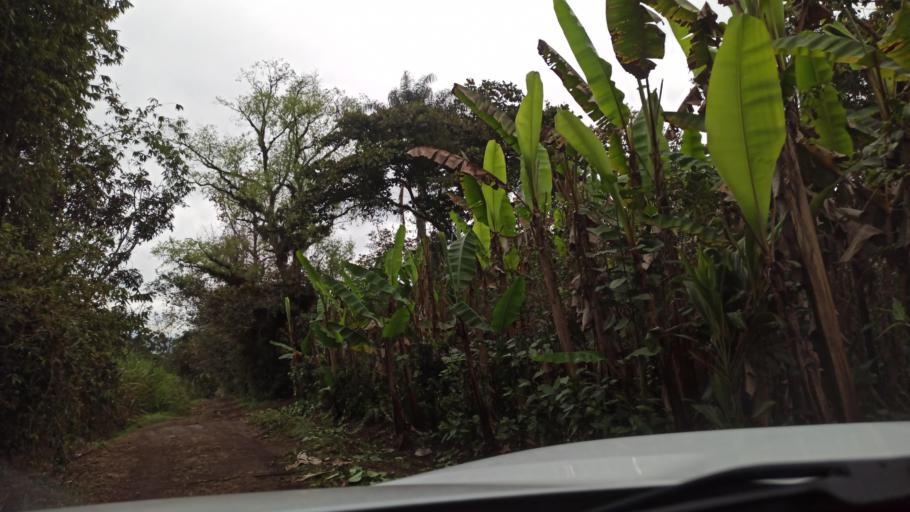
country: MX
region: Veracruz
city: Monte Blanco
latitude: 18.9794
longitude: -97.0085
